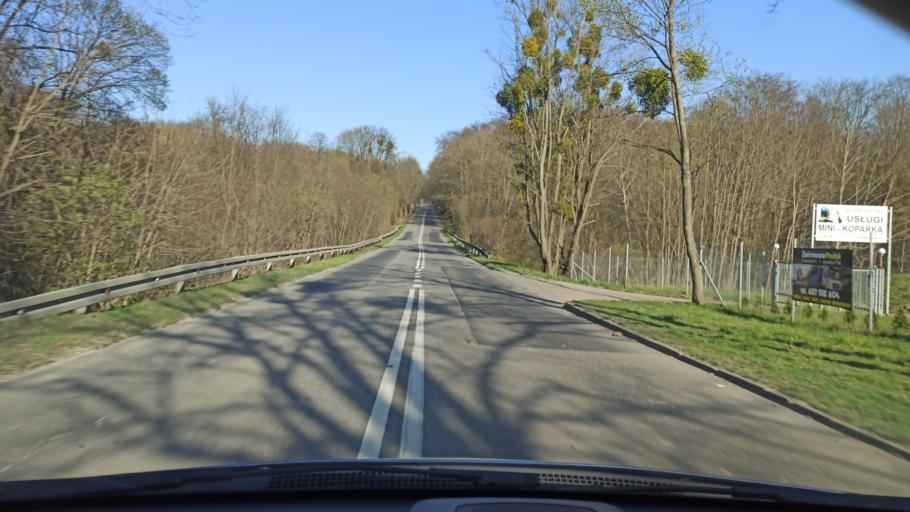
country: PL
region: Warmian-Masurian Voivodeship
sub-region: Powiat elblaski
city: Gronowo Gorne
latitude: 54.1843
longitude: 19.4476
